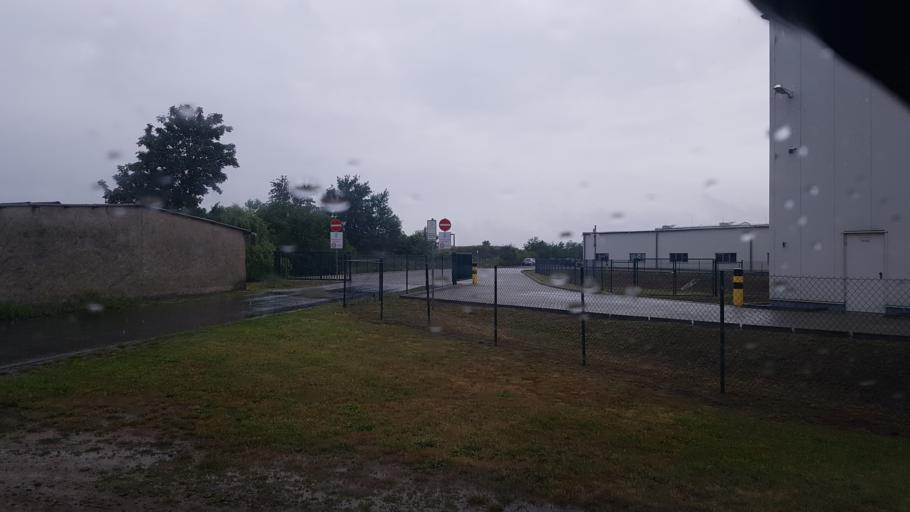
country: DE
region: Brandenburg
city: Dahme
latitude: 51.8666
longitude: 13.4121
